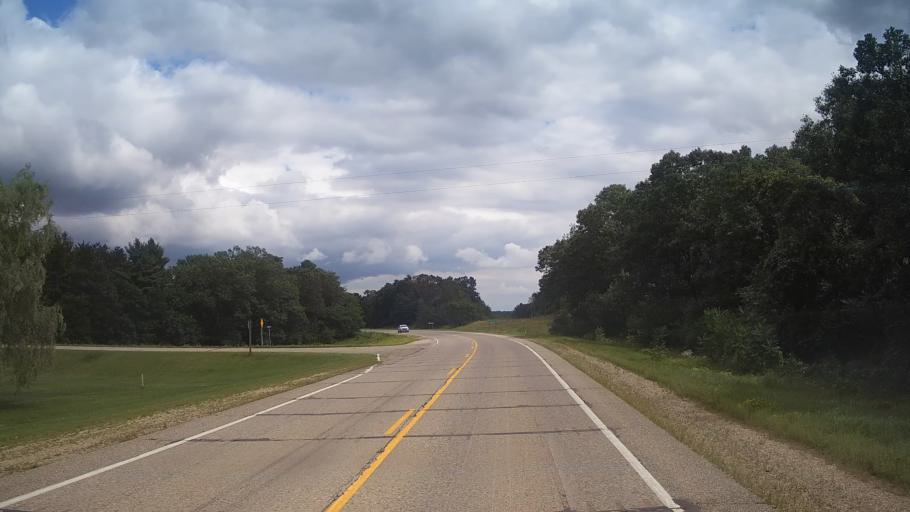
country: US
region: Wisconsin
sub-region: Marquette County
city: Westfield
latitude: 44.0218
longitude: -89.5478
